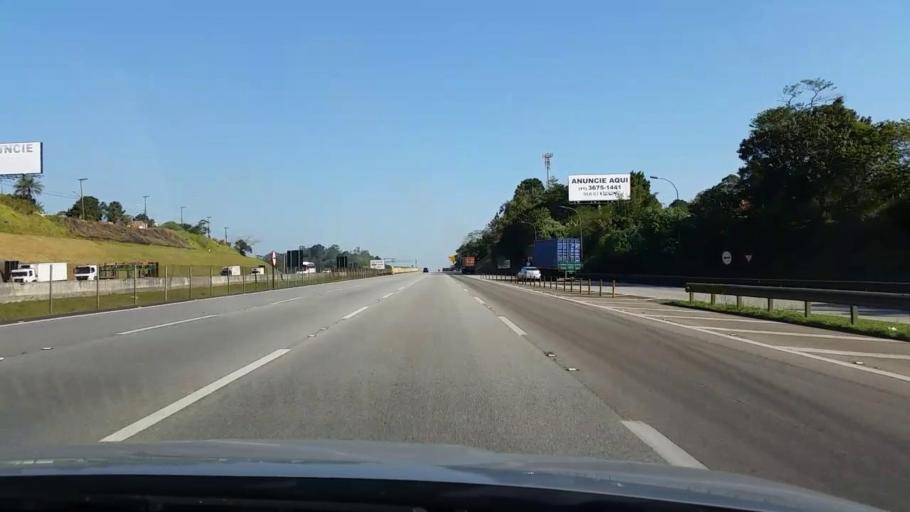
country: BR
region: Sao Paulo
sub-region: Sao Bernardo Do Campo
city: Sao Bernardo do Campo
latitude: -23.7725
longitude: -46.5938
